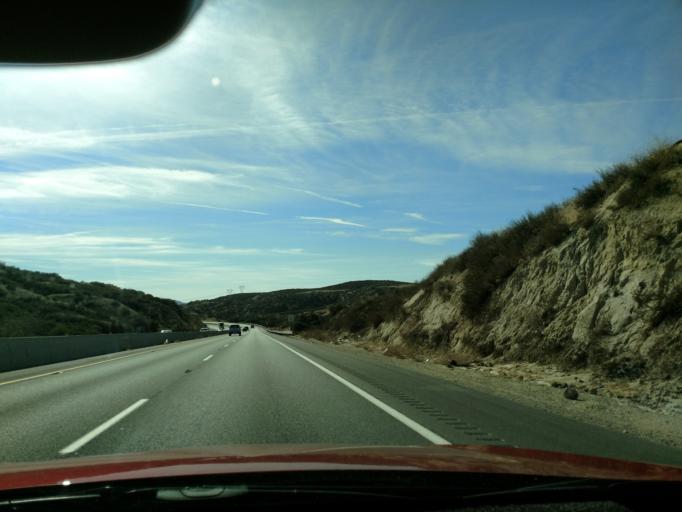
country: US
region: California
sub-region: Riverside County
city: Beaumont
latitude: 33.9076
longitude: -116.9829
